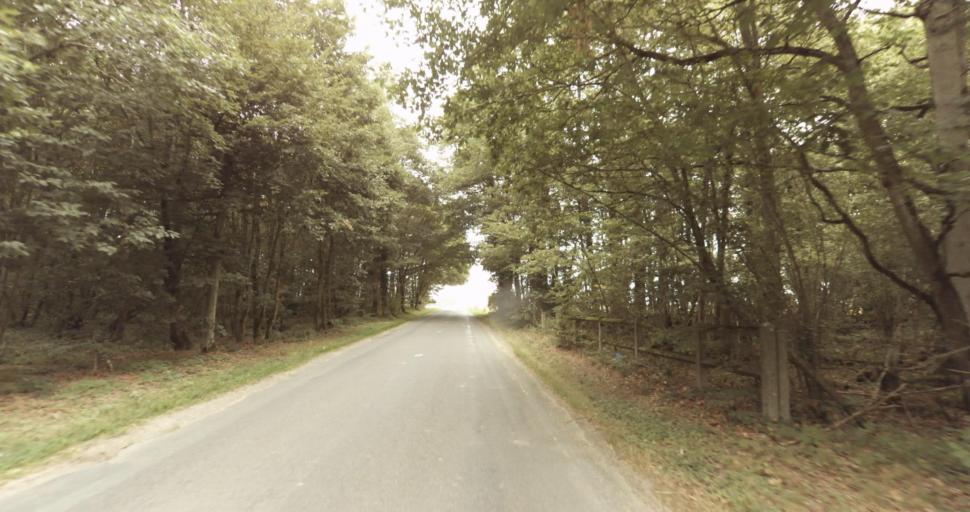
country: FR
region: Haute-Normandie
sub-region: Departement de l'Eure
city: Saint-Germain-sur-Avre
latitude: 48.8010
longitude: 1.2749
